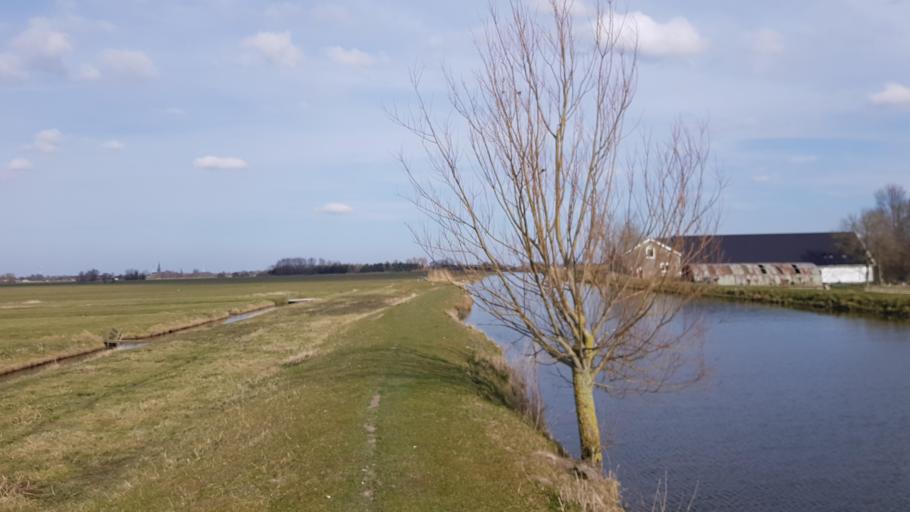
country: NL
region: South Holland
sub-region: Gemeente Zoetermeer
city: Zoetermeer
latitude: 52.0953
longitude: 4.4813
